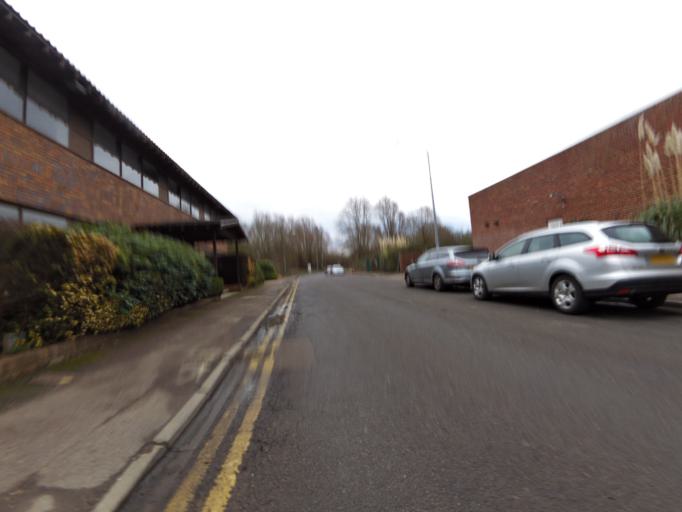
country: GB
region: England
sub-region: Cambridgeshire
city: Waterbeach
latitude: 52.2374
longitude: 0.1581
